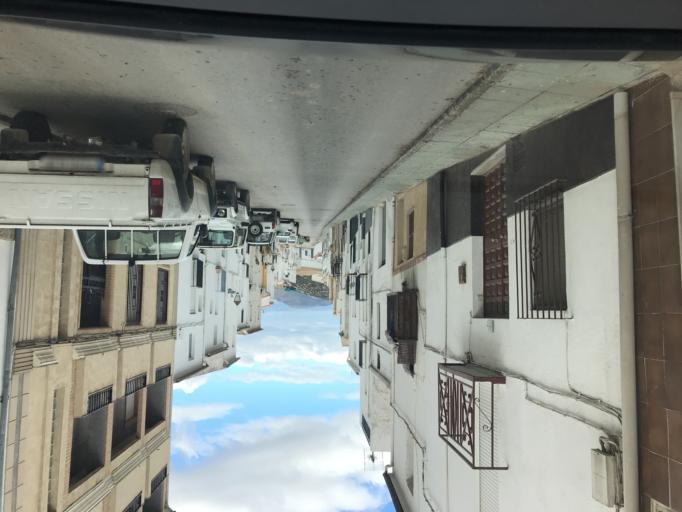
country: ES
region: Andalusia
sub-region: Provincia de Jaen
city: Torres
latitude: 37.7931
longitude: -3.4655
